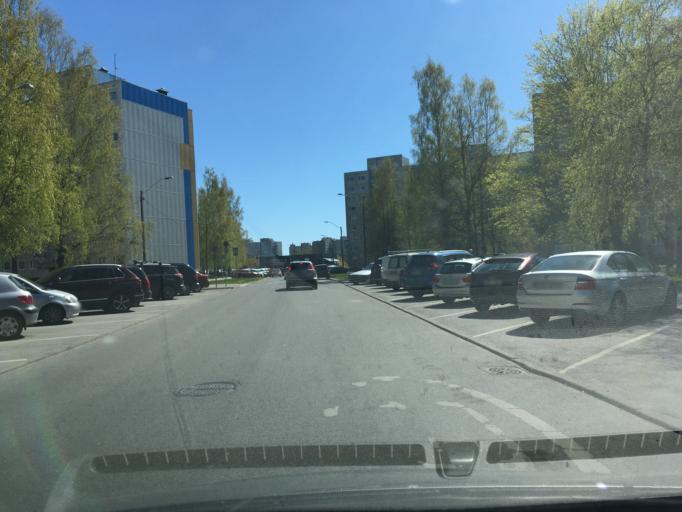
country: EE
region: Harju
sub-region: Tallinna linn
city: Kose
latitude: 59.4450
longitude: 24.8694
